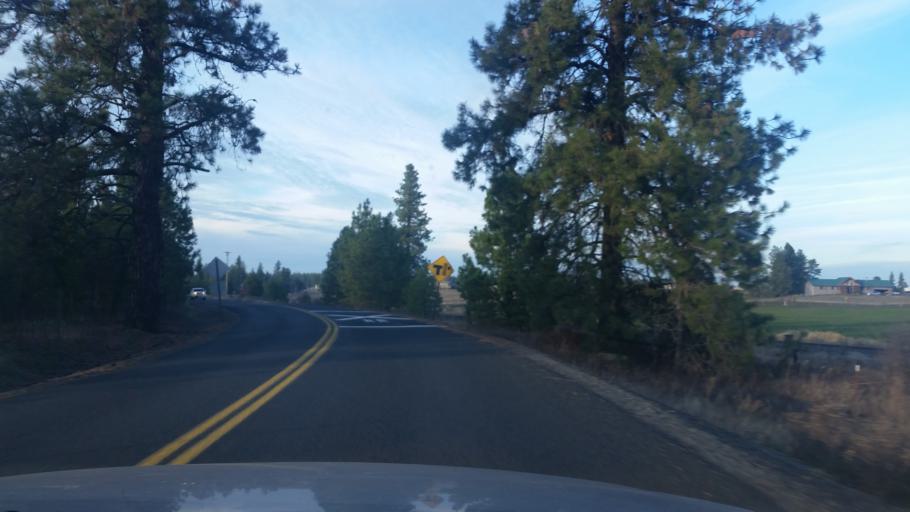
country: US
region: Washington
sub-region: Spokane County
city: Cheney
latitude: 47.5138
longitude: -117.4710
